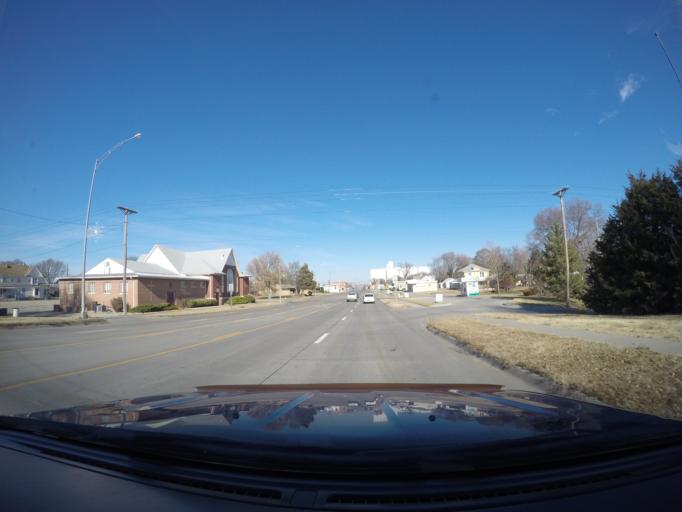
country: US
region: Kansas
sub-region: Cloud County
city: Concordia
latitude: 39.5687
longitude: -97.6574
